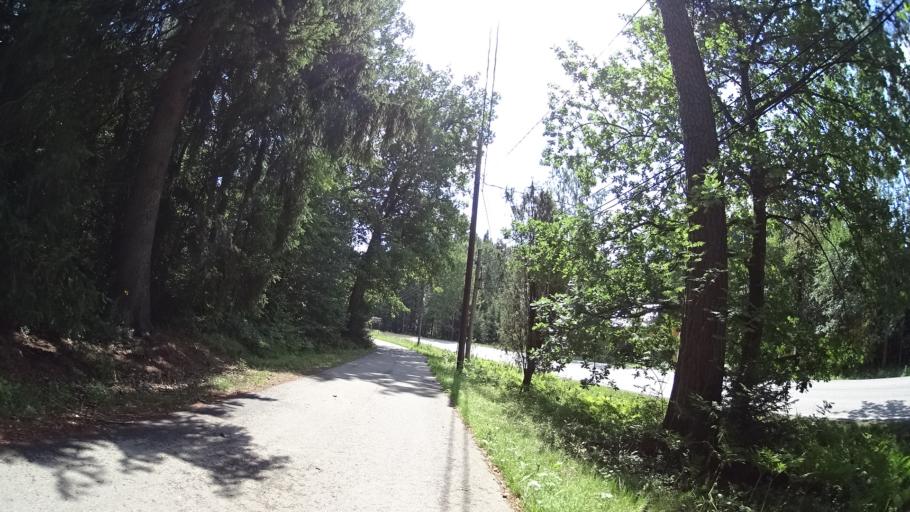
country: FI
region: Uusimaa
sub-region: Helsinki
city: Tuusula
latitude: 60.3621
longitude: 24.9869
